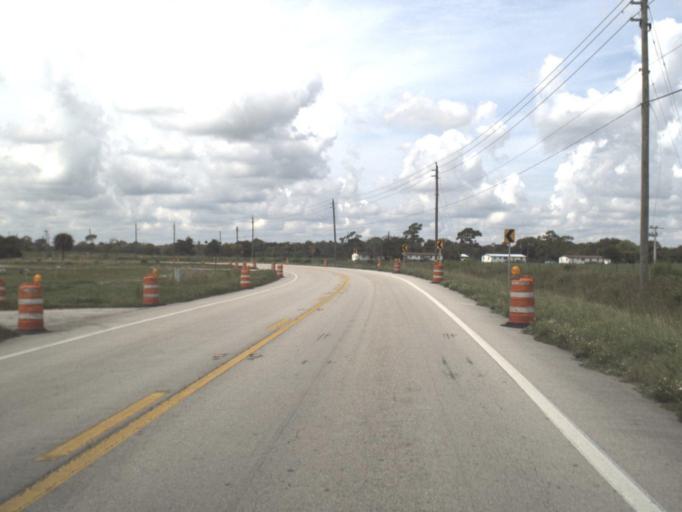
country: US
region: Florida
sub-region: Okeechobee County
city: Taylor Creek
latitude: 27.2577
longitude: -80.7560
